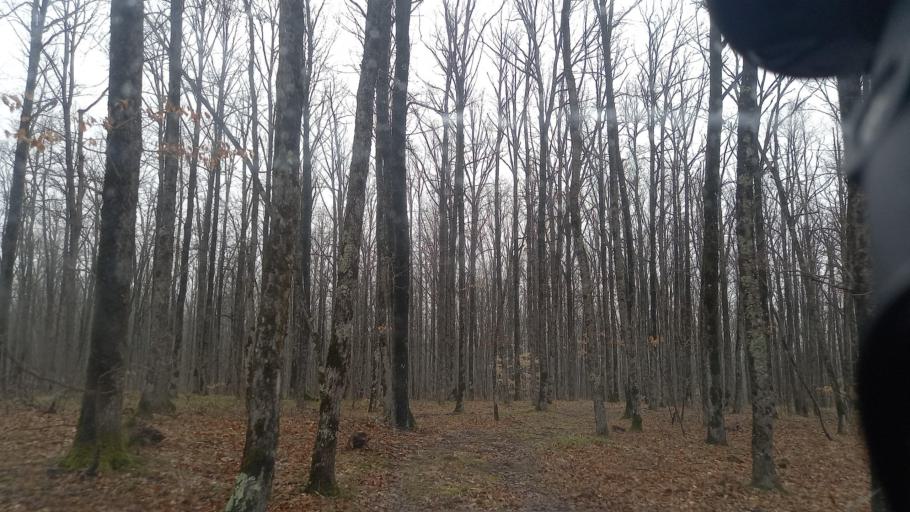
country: RU
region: Krasnodarskiy
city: Saratovskaya
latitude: 44.6526
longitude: 39.2404
